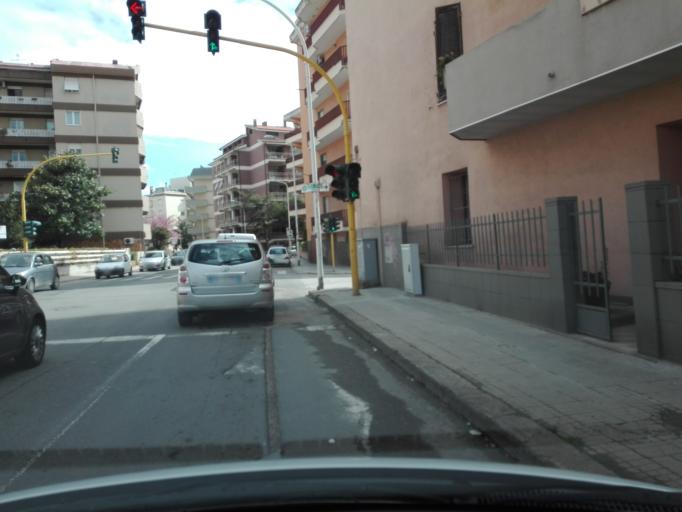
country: IT
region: Sardinia
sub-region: Provincia di Sassari
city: Sassari
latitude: 40.7279
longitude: 8.5754
